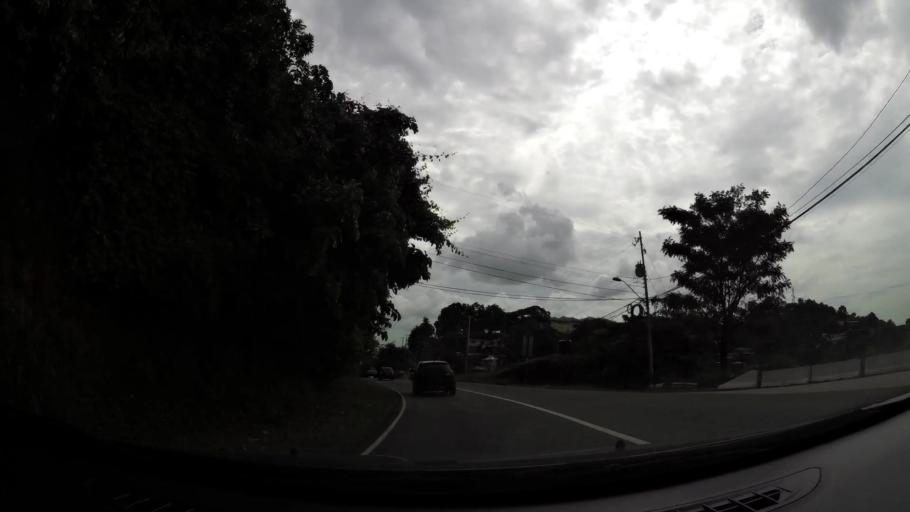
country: TT
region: San Juan/Laventille
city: Laventille
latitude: 10.6697
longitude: -61.4908
